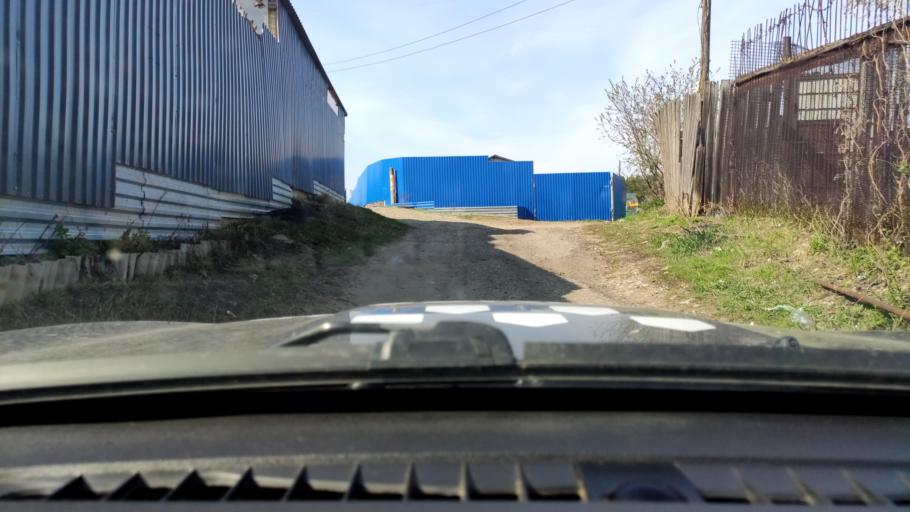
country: RU
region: Samara
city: Zhigulevsk
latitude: 53.4968
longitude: 49.4947
